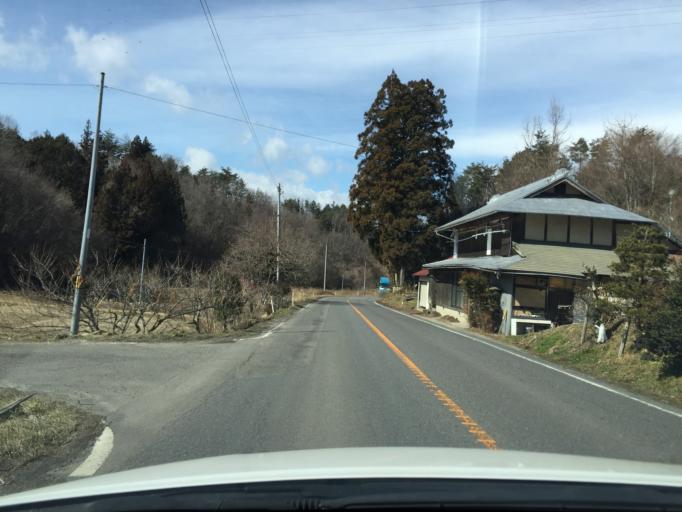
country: JP
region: Fukushima
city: Funehikimachi-funehiki
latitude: 37.4026
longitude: 140.5499
